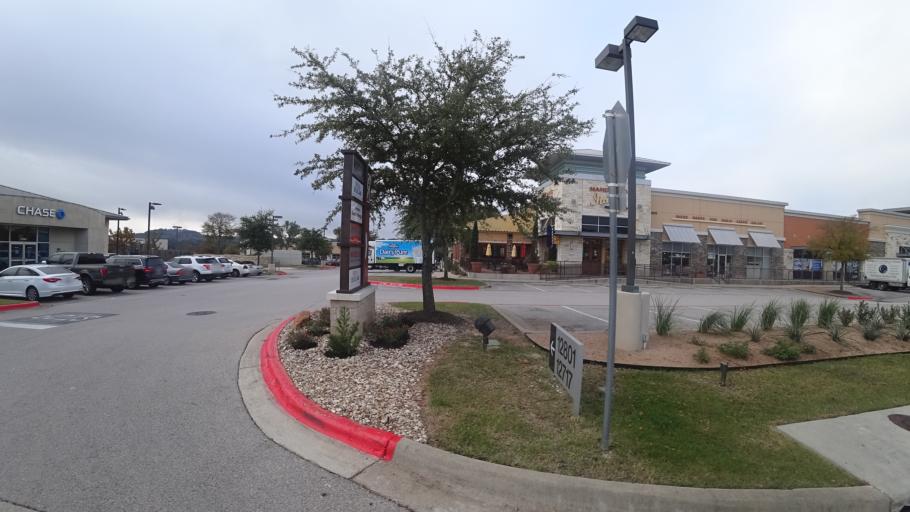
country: US
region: Texas
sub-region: Travis County
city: Bee Cave
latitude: 30.3053
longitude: -97.9417
